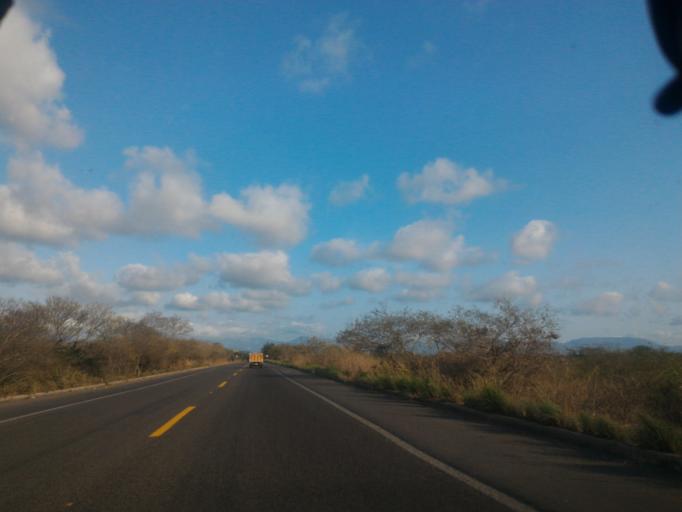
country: MX
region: Michoacan
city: Coahuayana Viejo
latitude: 18.7824
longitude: -103.7695
